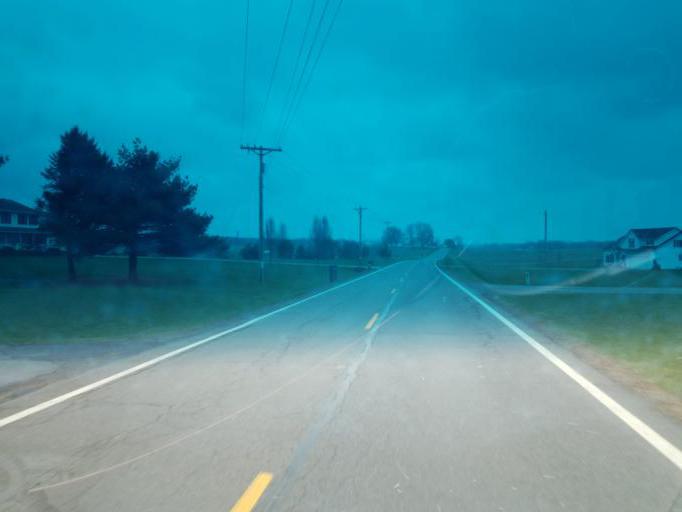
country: US
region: Ohio
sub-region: Knox County
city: Fredericktown
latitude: 40.4685
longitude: -82.6504
